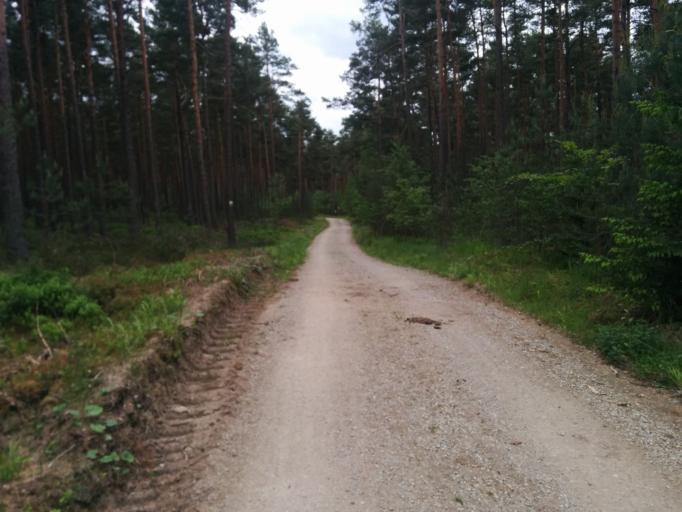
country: DE
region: Bavaria
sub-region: Regierungsbezirk Mittelfranken
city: Uttenreuth
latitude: 49.5453
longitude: 11.0761
